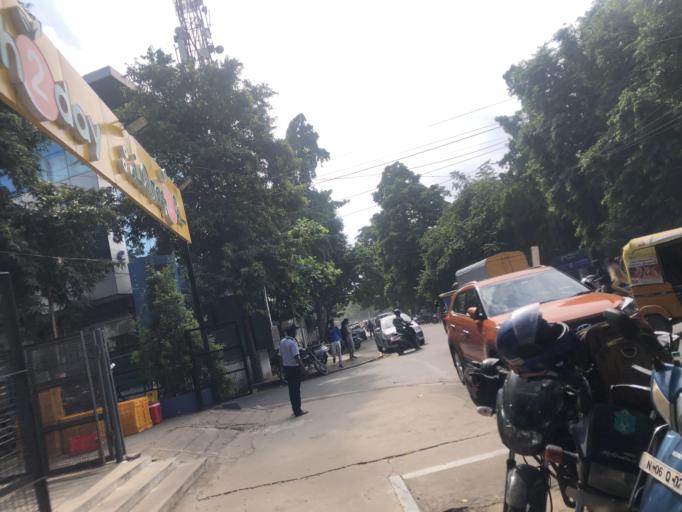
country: IN
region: Tamil Nadu
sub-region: Chennai
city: Gandhi Nagar
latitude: 13.0375
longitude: 80.2630
